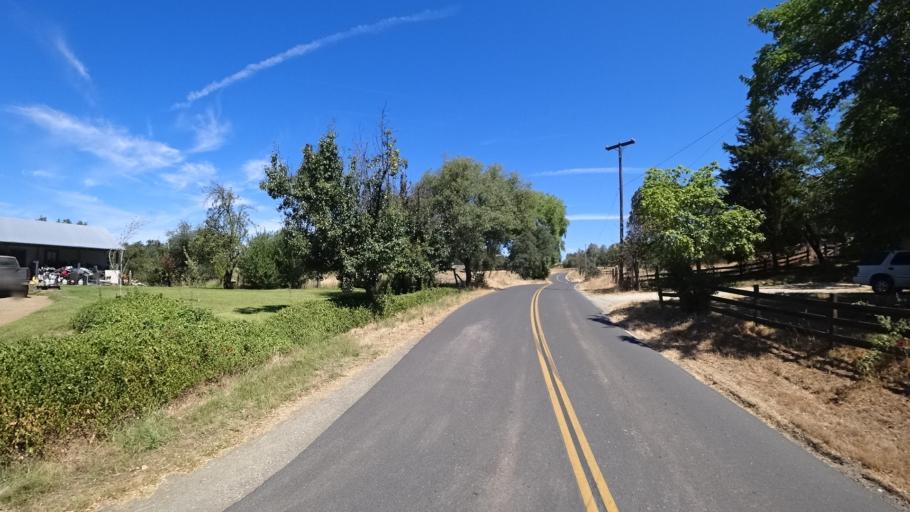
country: US
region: California
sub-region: Calaveras County
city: Angels Camp
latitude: 38.0880
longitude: -120.5565
